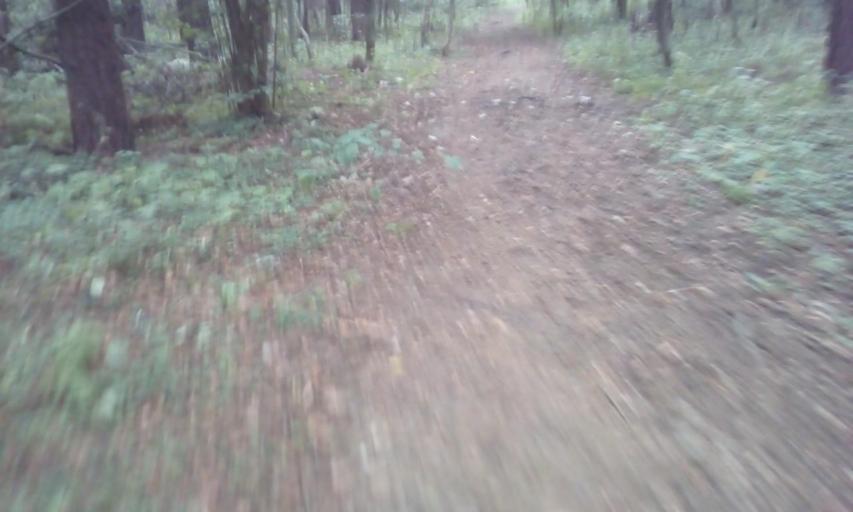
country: RU
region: Moskovskaya
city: Zhavoronki
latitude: 55.6632
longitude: 37.1244
